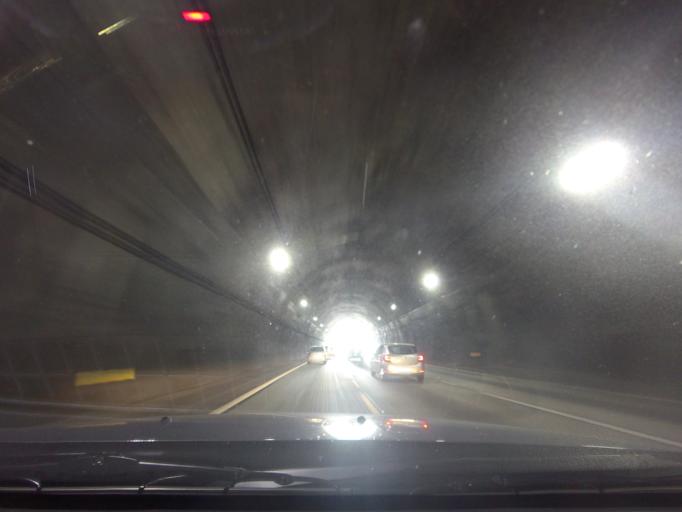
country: BR
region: Sao Paulo
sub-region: Cubatao
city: Cubatao
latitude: -23.9175
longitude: -46.5241
